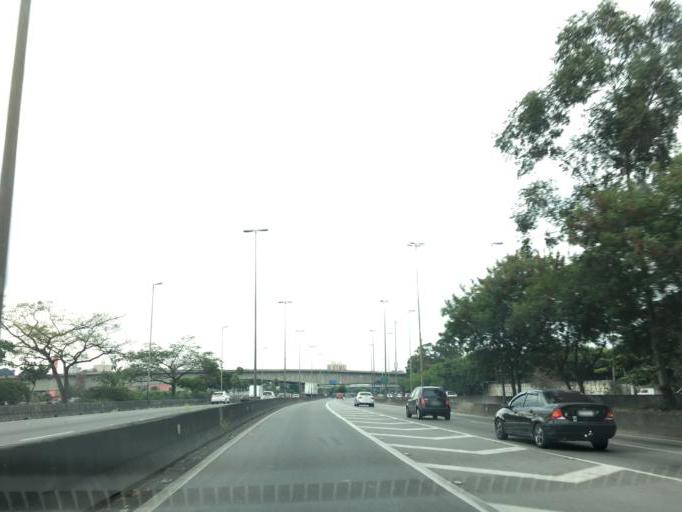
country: BR
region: Sao Paulo
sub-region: Osasco
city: Osasco
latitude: -23.5230
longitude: -46.7474
